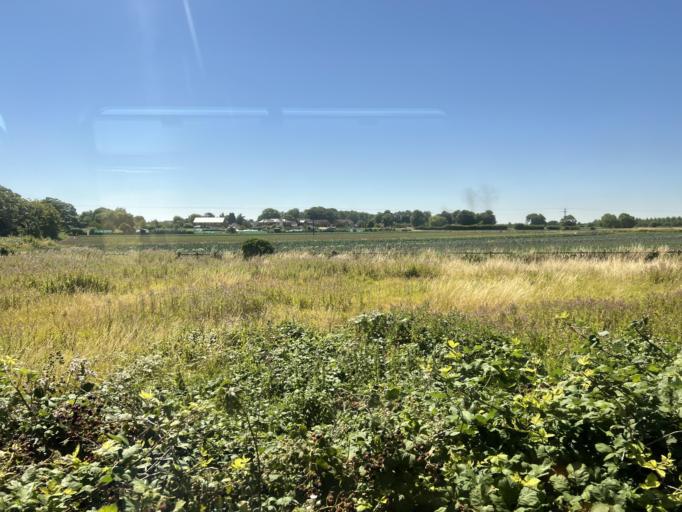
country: GB
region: England
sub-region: Lincolnshire
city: Wainfleet All Saints
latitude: 53.1071
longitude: 0.2304
